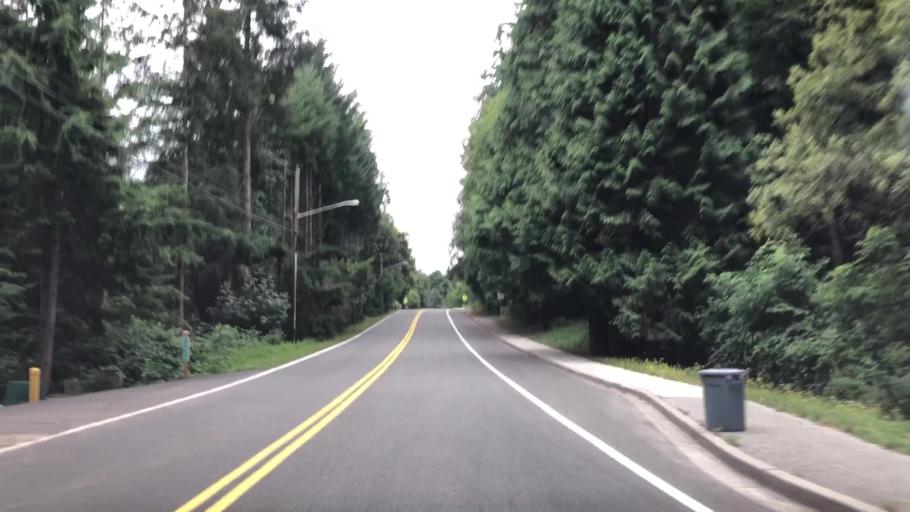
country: US
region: Washington
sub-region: King County
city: Woodinville
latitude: 47.7847
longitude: -122.1568
